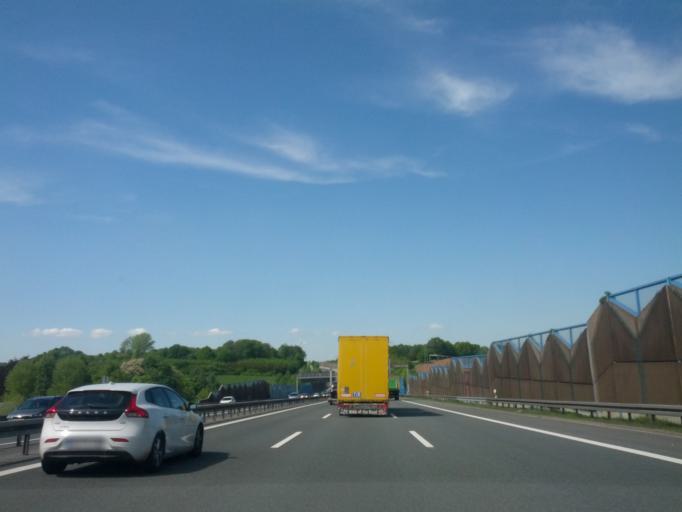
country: DE
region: Saxony
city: Neukirchen
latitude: 50.8170
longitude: 12.8574
